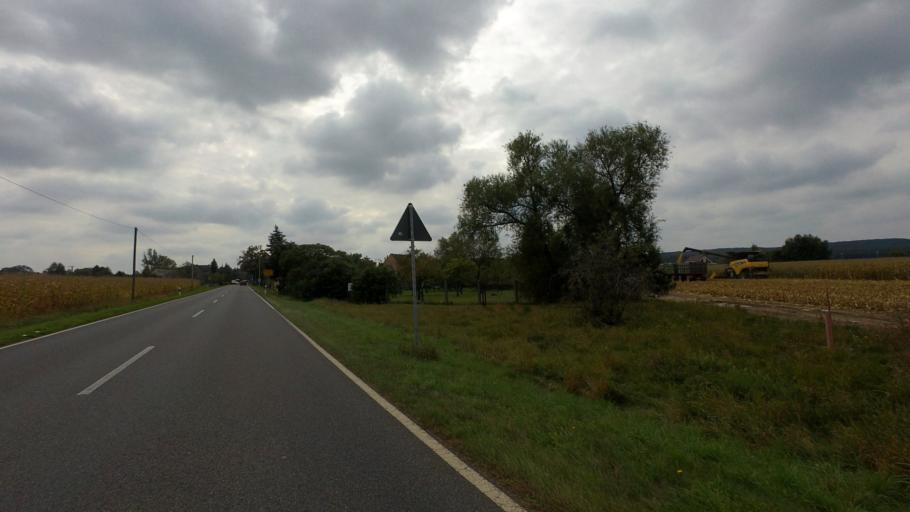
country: DE
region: Brandenburg
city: Luckau
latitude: 51.7773
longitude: 13.6887
